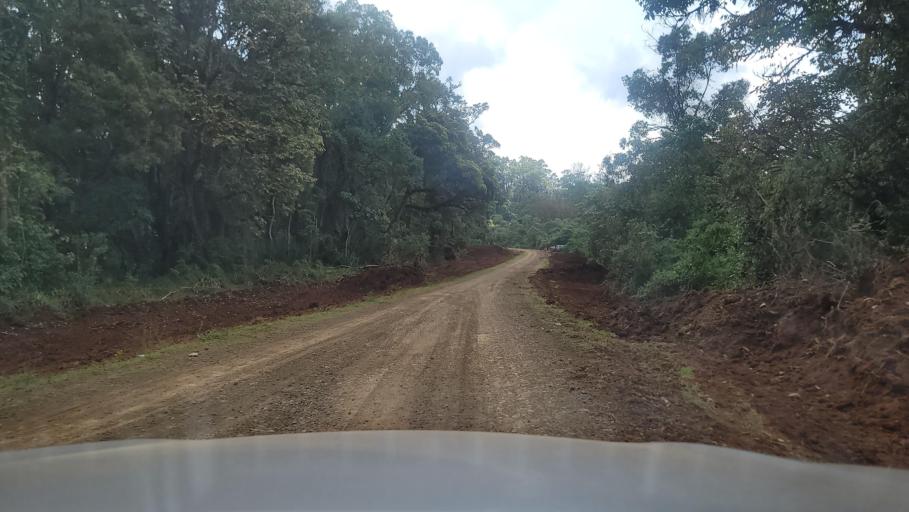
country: ET
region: Southern Nations, Nationalities, and People's Region
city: Bonga
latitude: 7.6610
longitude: 36.2470
